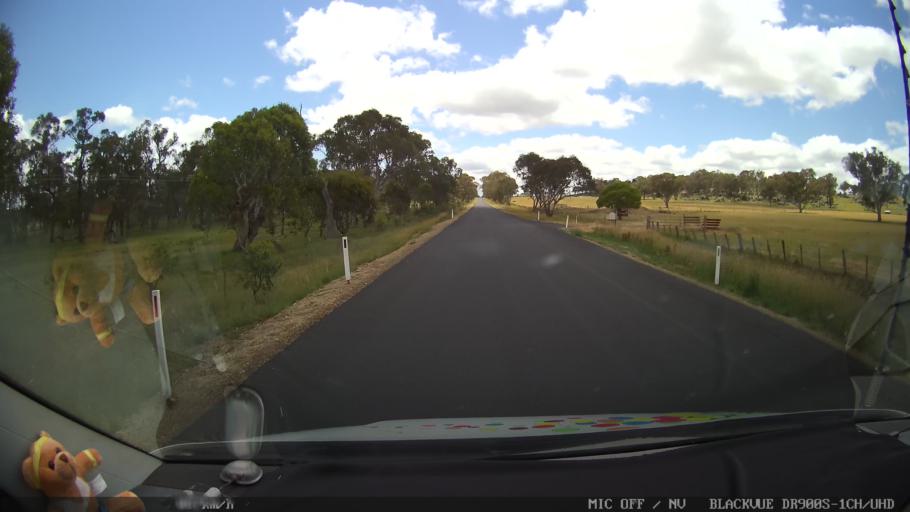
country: AU
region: New South Wales
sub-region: Glen Innes Severn
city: Glen Innes
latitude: -29.4240
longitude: 151.7065
